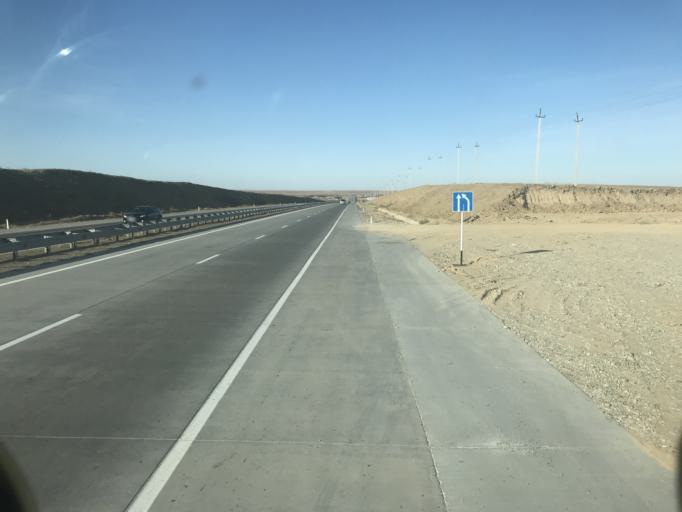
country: KZ
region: Ongtustik Qazaqstan
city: Temirlanovka
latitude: 42.5715
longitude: 69.3105
